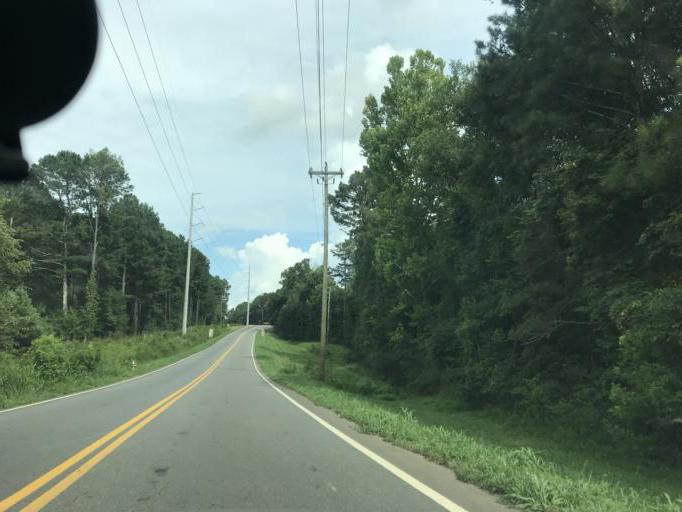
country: US
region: Georgia
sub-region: Forsyth County
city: Cumming
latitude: 34.3076
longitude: -84.2182
